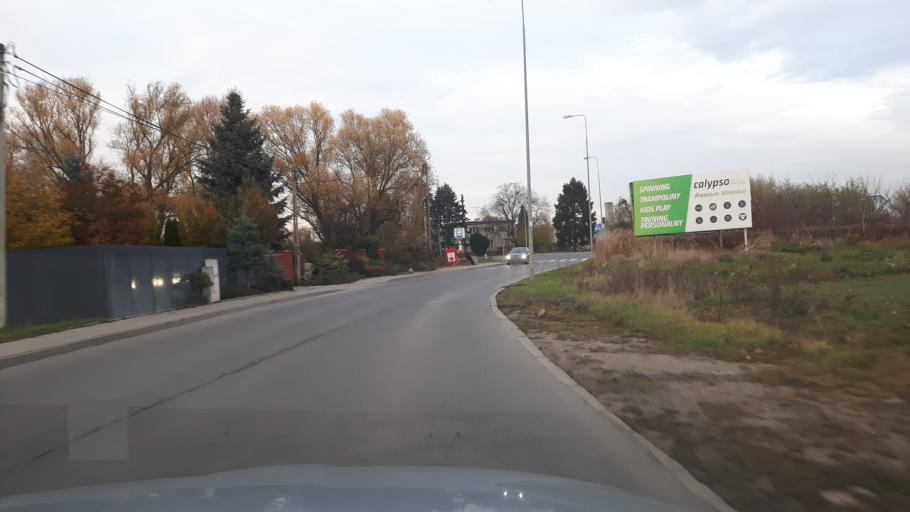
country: PL
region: Masovian Voivodeship
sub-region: Warszawa
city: Wilanow
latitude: 52.1758
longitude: 21.1071
